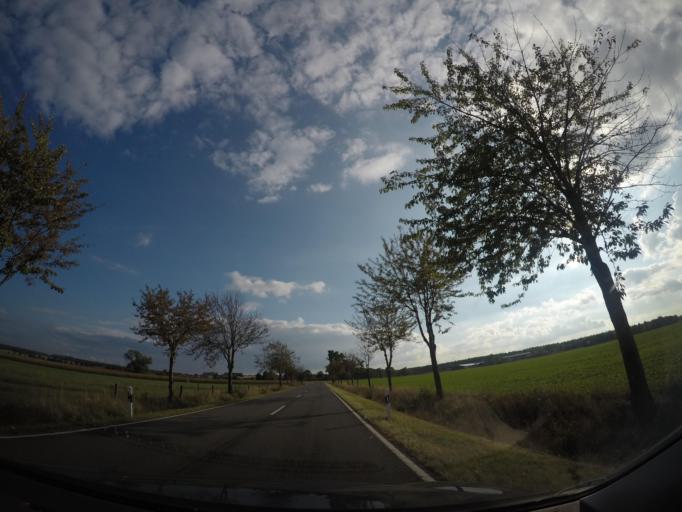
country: DE
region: Saxony-Anhalt
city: Weferlingen
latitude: 52.3743
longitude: 11.0986
